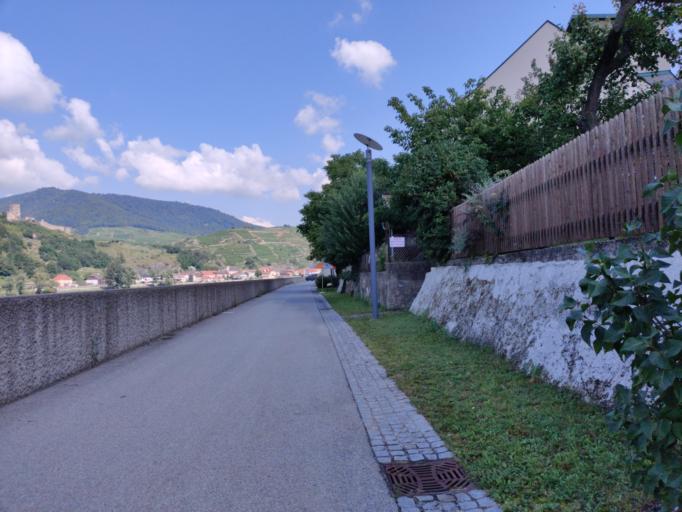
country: AT
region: Lower Austria
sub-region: Politischer Bezirk Krems
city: Spitz
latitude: 48.3527
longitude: 15.4110
